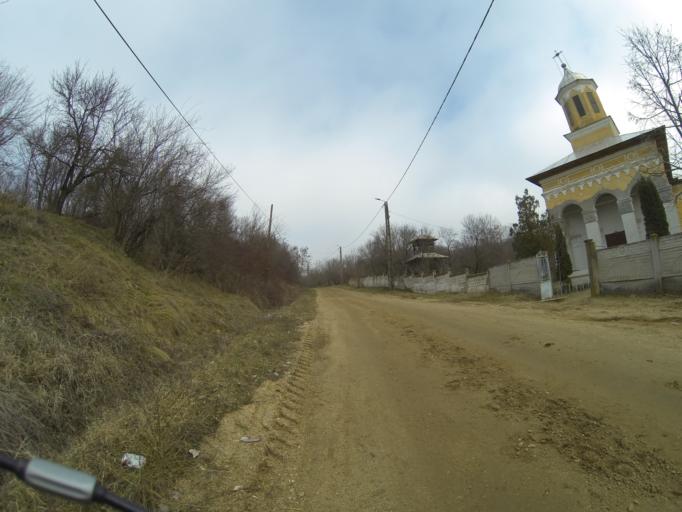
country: RO
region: Mehedinti
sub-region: Comuna Poroina Mare
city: Poroina Mare
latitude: 44.4930
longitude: 23.0003
